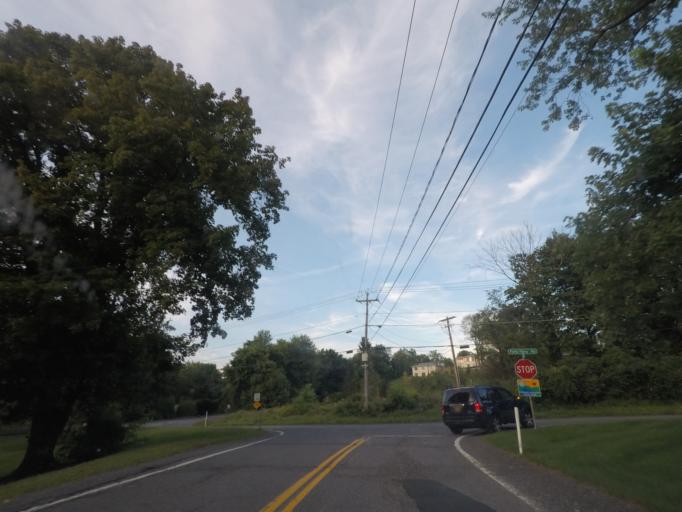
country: US
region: New York
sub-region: Schenectady County
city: Niskayuna
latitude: 42.7802
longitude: -73.7890
